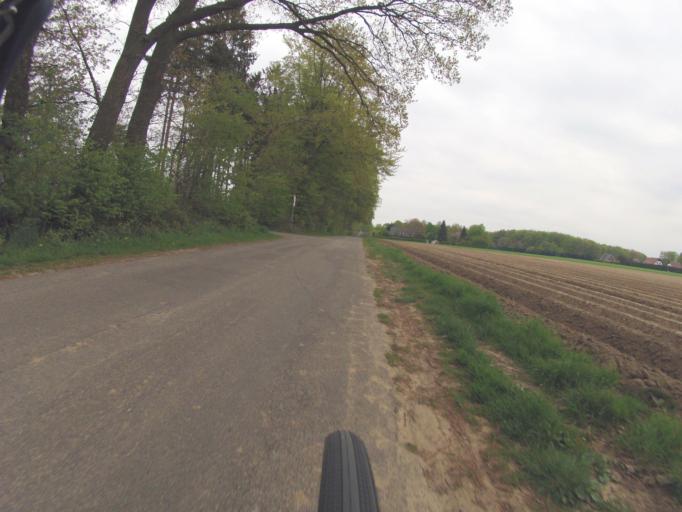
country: DE
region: North Rhine-Westphalia
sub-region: Regierungsbezirk Munster
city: Mettingen
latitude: 52.2971
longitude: 7.7886
